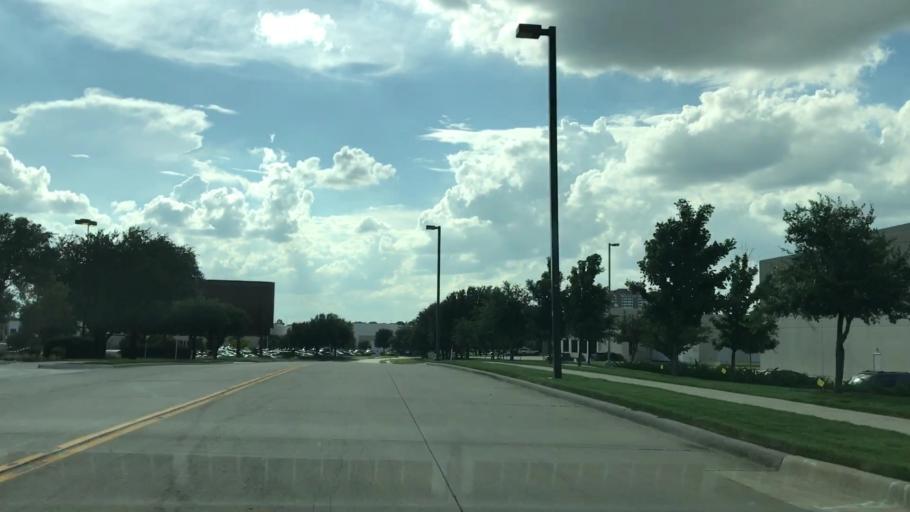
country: US
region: Texas
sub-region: Dallas County
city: Coppell
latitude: 32.9150
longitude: -97.0004
